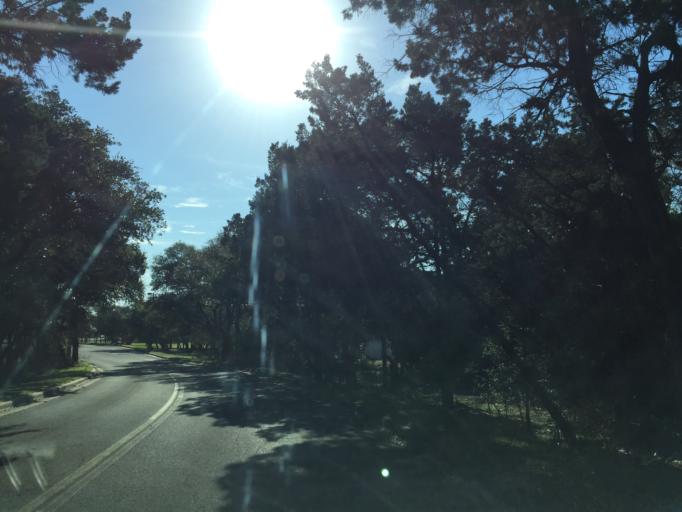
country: US
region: Texas
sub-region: Williamson County
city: Jollyville
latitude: 30.3942
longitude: -97.7367
